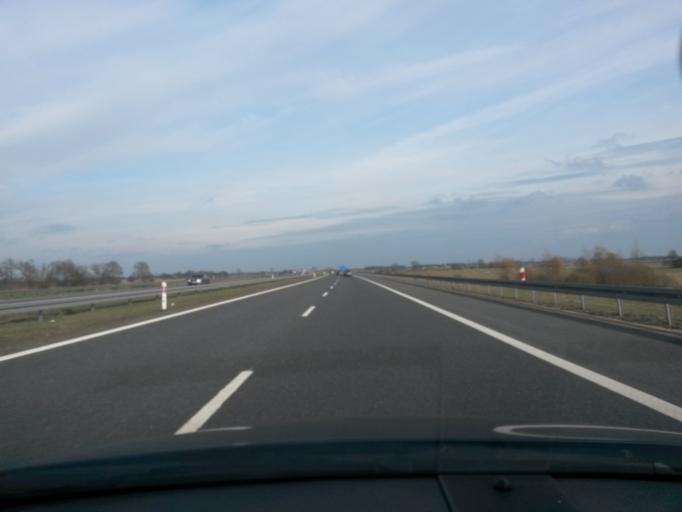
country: PL
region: Lodz Voivodeship
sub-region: Powiat poddebicki
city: Wartkowice
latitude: 52.0003
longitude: 19.0033
